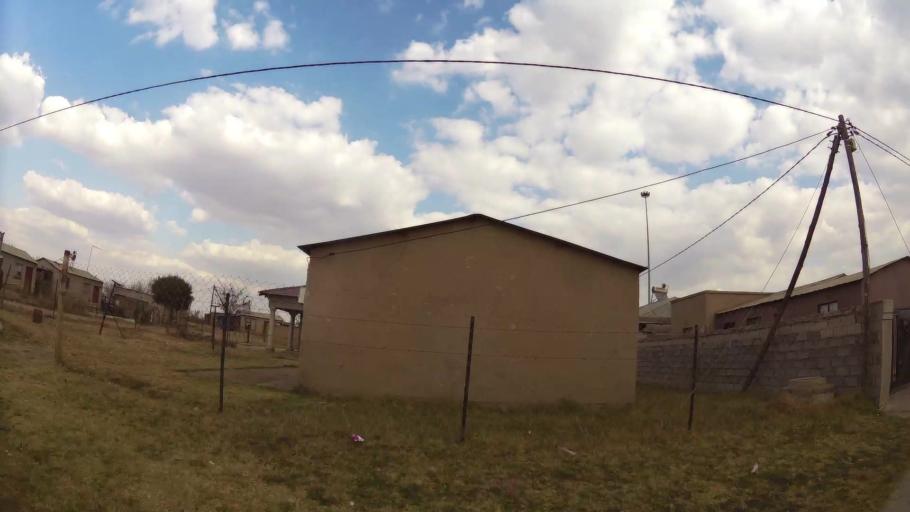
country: ZA
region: Mpumalanga
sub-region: Nkangala District Municipality
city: Delmas
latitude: -26.1435
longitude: 28.6933
